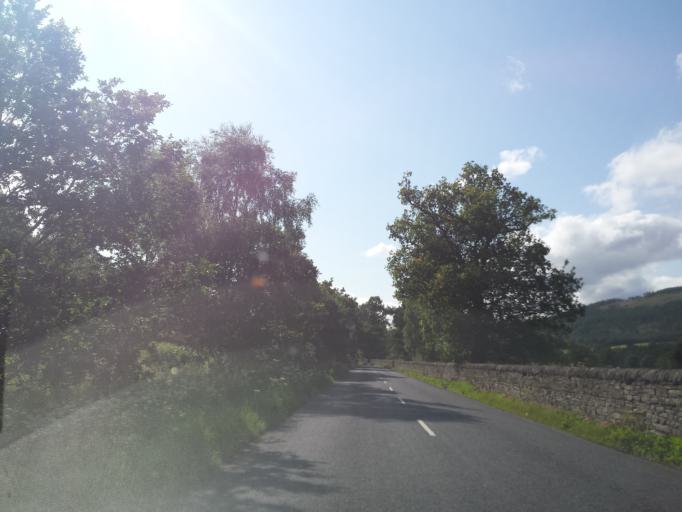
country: GB
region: Scotland
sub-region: Perth and Kinross
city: Pitlochry
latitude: 56.7668
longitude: -3.8610
